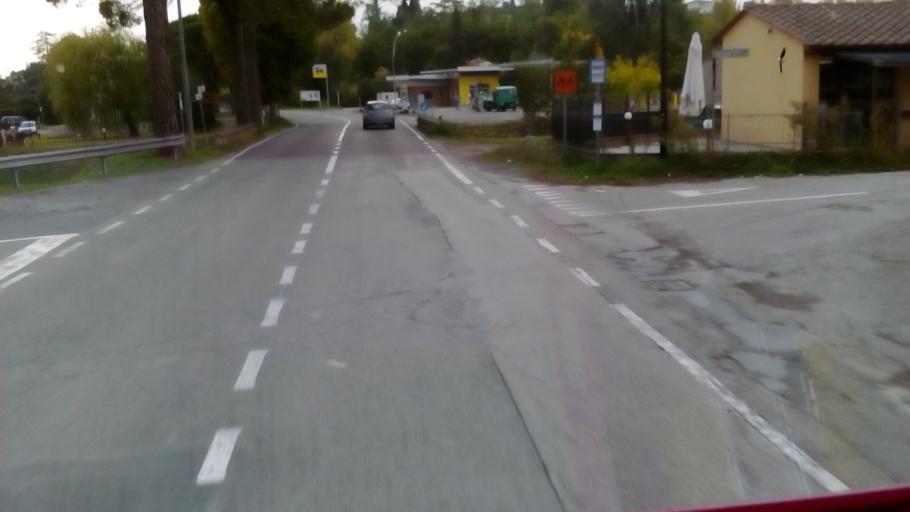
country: IT
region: Tuscany
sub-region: Province of Florence
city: Castelfiorentino
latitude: 43.6143
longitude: 10.9680
